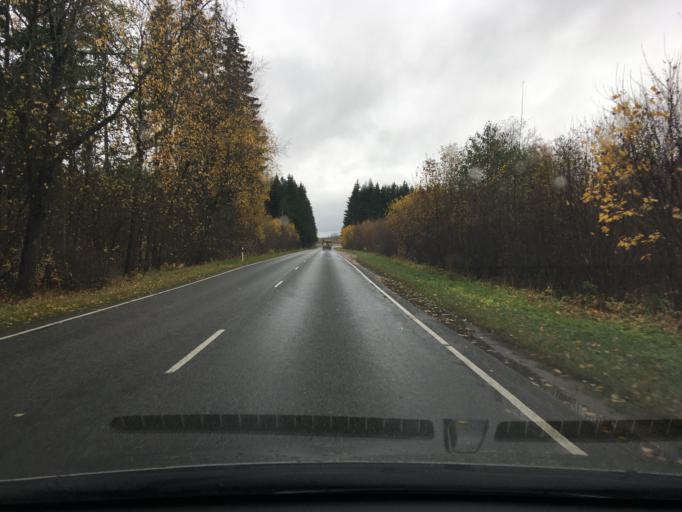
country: EE
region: Jogevamaa
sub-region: Tabivere vald
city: Tabivere
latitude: 58.4618
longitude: 26.6442
